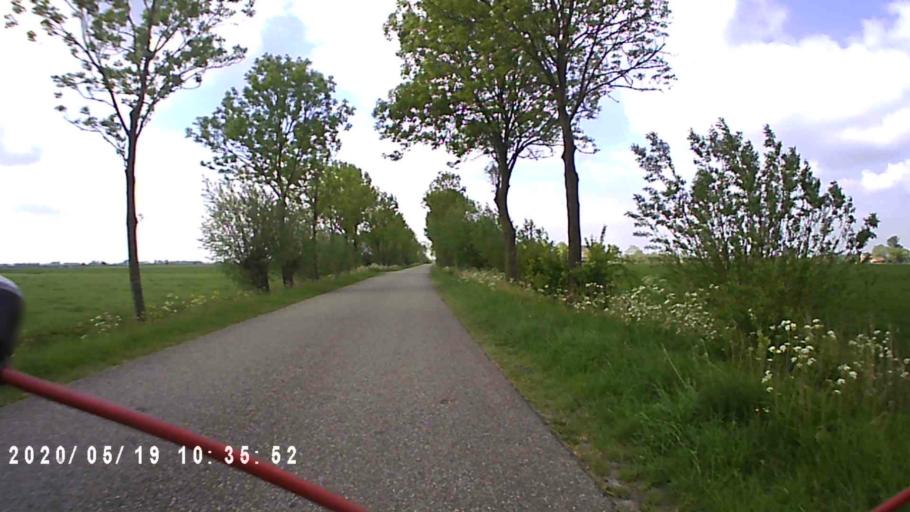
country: NL
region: Friesland
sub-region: Gemeente Kollumerland en Nieuwkruisland
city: Kollum
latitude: 53.2796
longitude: 6.1841
